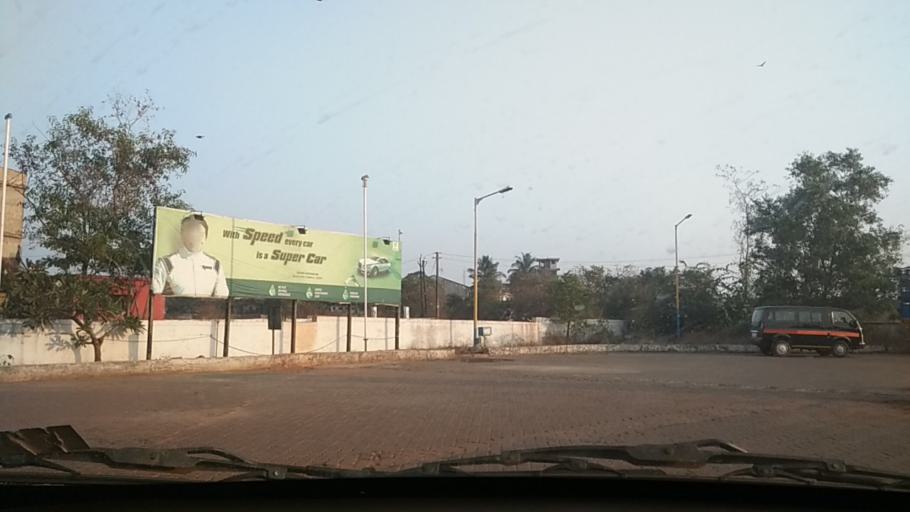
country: IN
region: Goa
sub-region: South Goa
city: Sancoale
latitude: 15.3785
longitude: 73.9262
